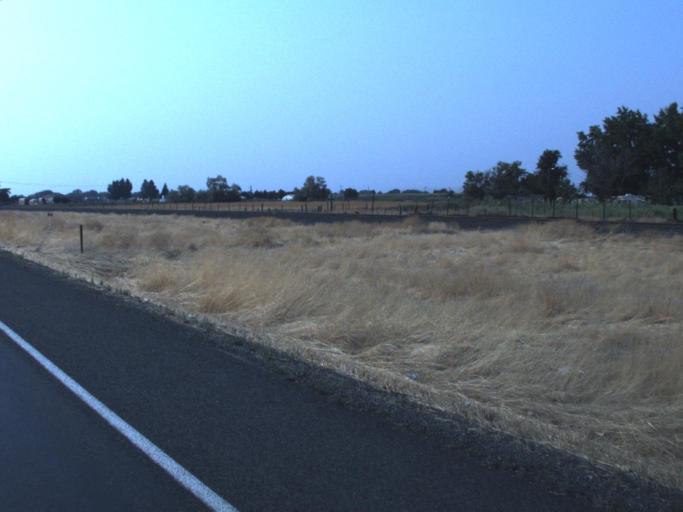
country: US
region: Washington
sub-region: Yakima County
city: Mabton
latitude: 46.2059
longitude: -119.9761
